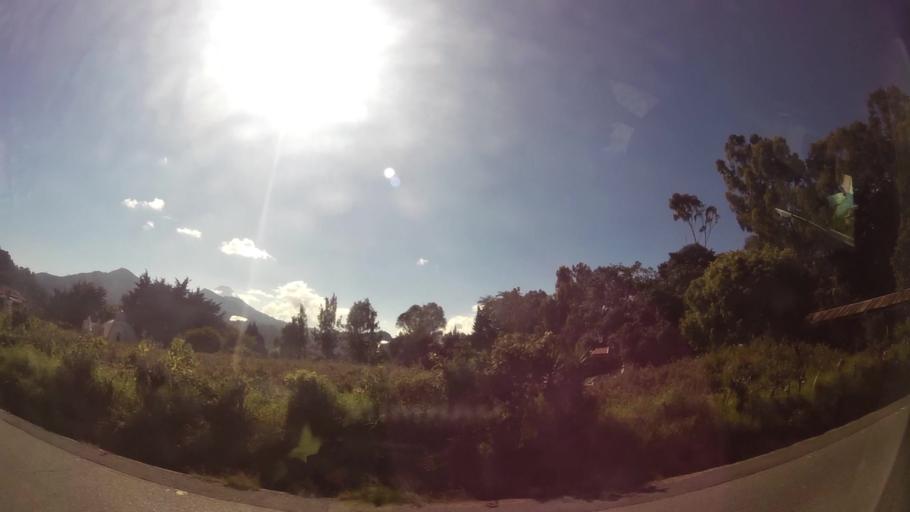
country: GT
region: Sacatepequez
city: Santa Lucia Milpas Altas
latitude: 14.5695
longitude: -90.6396
